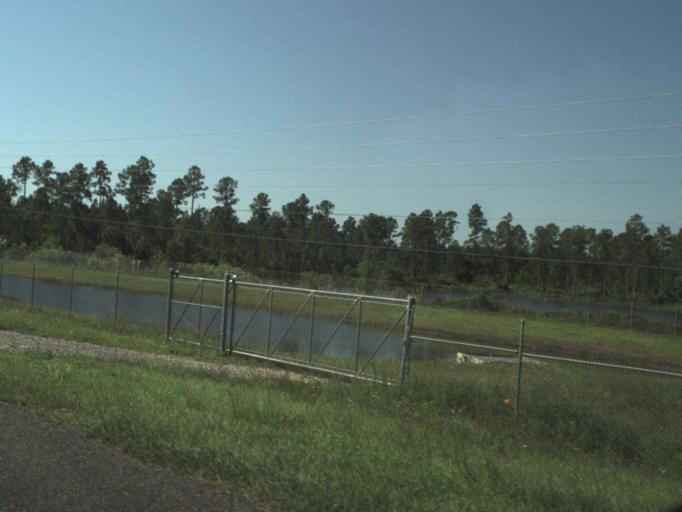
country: US
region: Florida
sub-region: Orange County
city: Christmas
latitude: 28.4416
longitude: -80.9708
